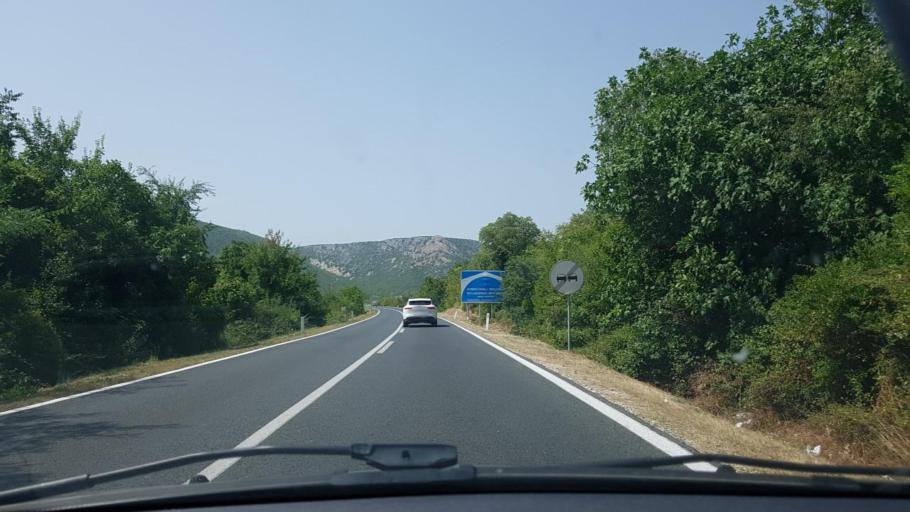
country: BA
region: Federation of Bosnia and Herzegovina
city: Crnici
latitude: 43.1809
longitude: 17.7857
